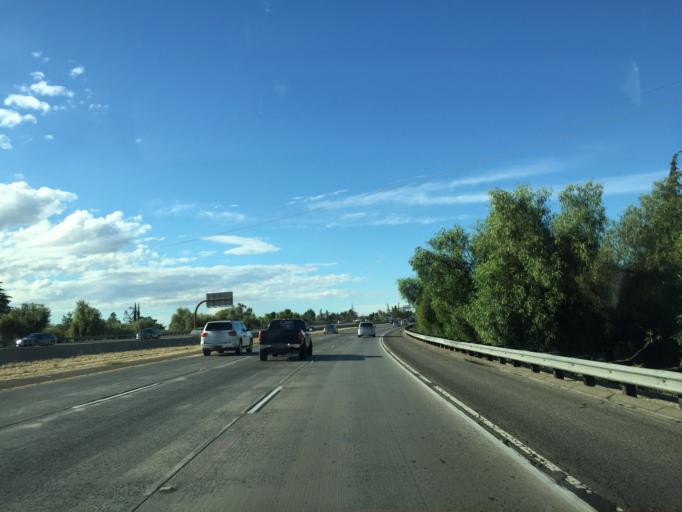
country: US
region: California
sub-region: Fresno County
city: Fresno
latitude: 36.7696
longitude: -119.7830
